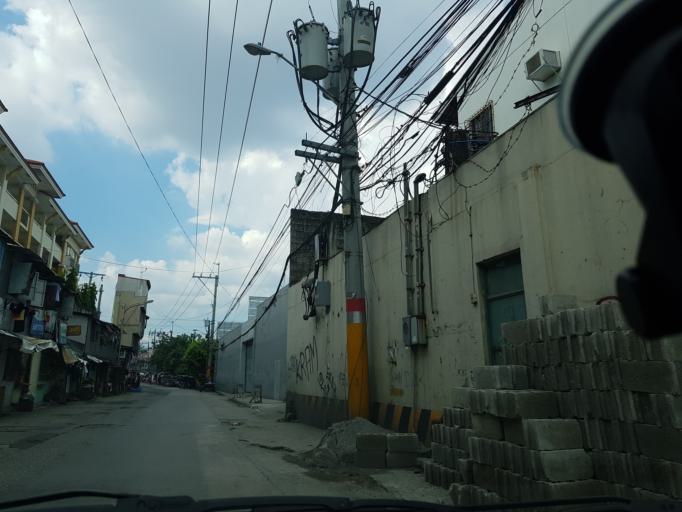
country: PH
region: Metro Manila
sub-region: Pasig
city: Pasig City
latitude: 14.5880
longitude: 121.0914
